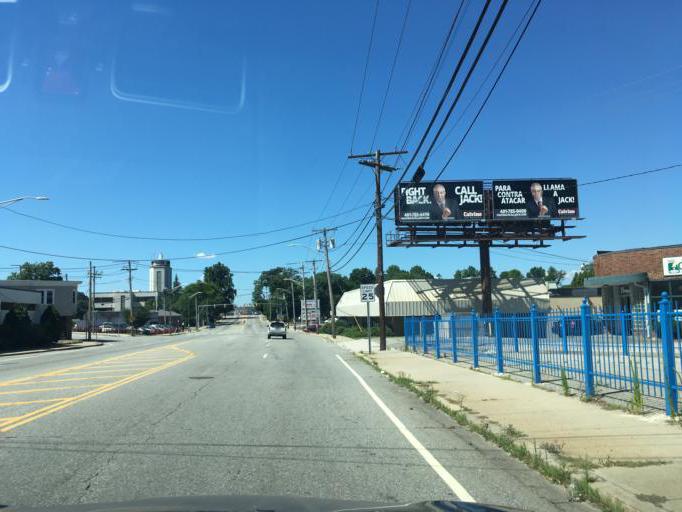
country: US
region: Rhode Island
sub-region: Providence County
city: Cranston
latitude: 41.7889
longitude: -71.4306
